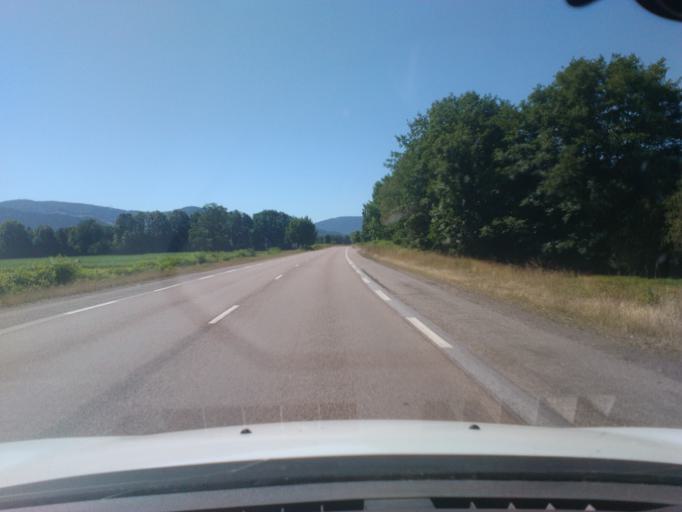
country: FR
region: Lorraine
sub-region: Departement des Vosges
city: Vagney
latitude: 48.0219
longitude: 6.7049
